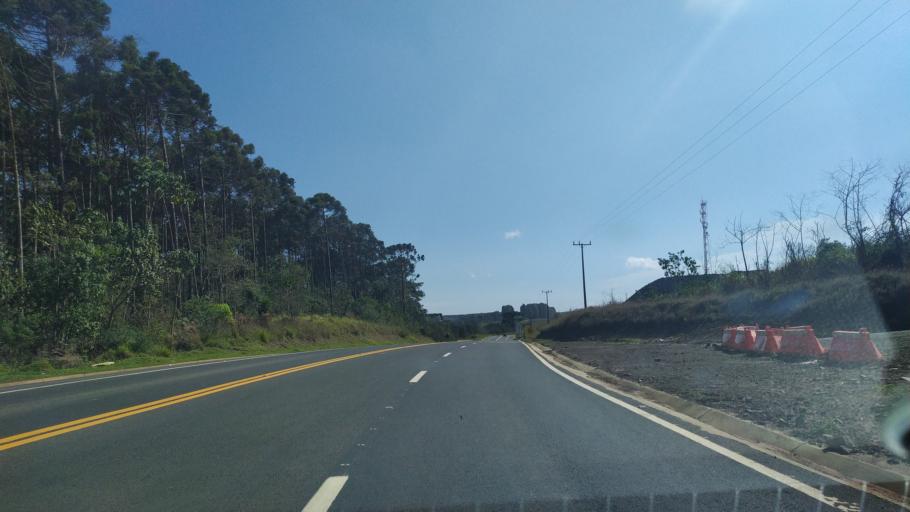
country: BR
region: Parana
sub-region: Telemaco Borba
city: Telemaco Borba
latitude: -24.2534
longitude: -50.7427
